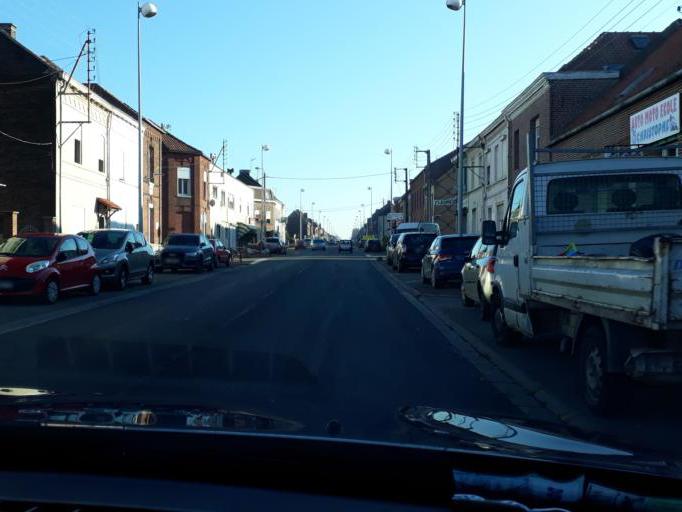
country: FR
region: Nord-Pas-de-Calais
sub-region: Departement du Nord
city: Aniche
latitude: 50.3274
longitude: 3.2472
